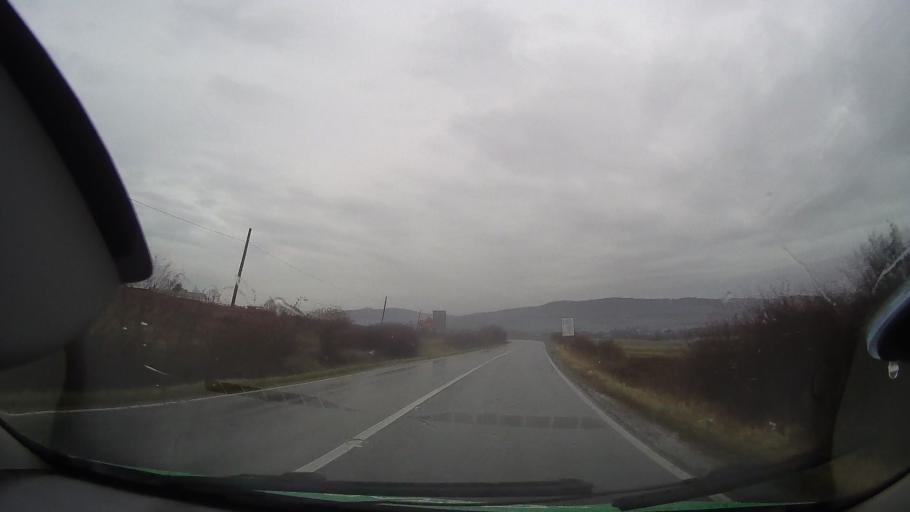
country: RO
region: Bihor
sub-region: Comuna Rabagani
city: Rabagani
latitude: 46.7406
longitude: 22.2289
